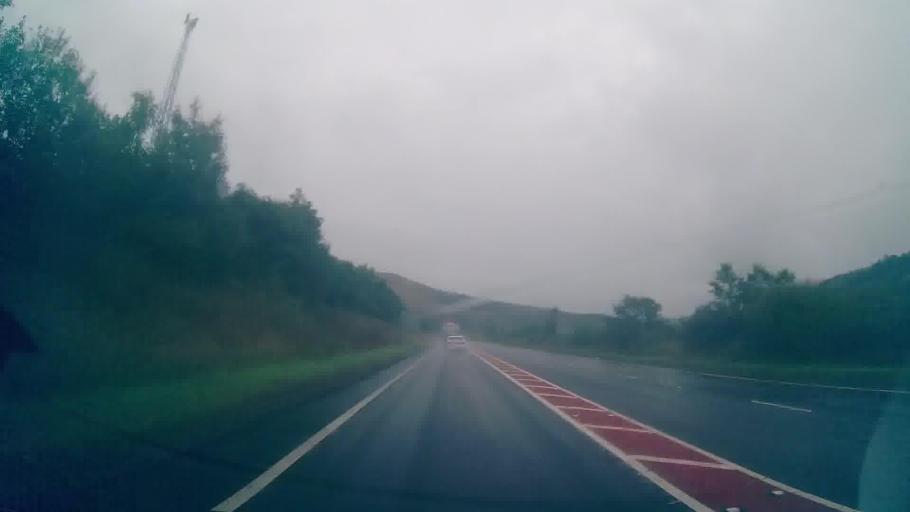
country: GB
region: Scotland
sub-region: Dumfries and Galloway
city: Sanquhar
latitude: 55.3433
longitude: -3.8574
